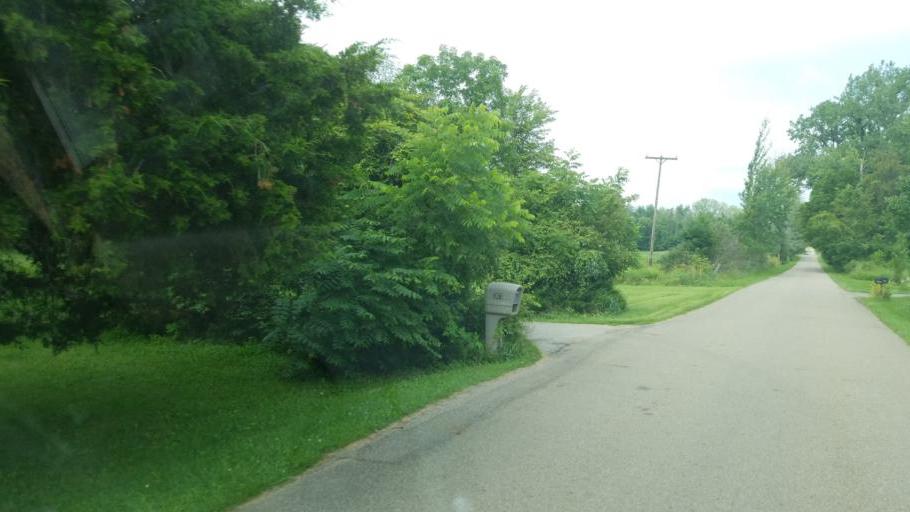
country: US
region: Ohio
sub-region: Licking County
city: Utica
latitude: 40.2202
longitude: -82.5552
